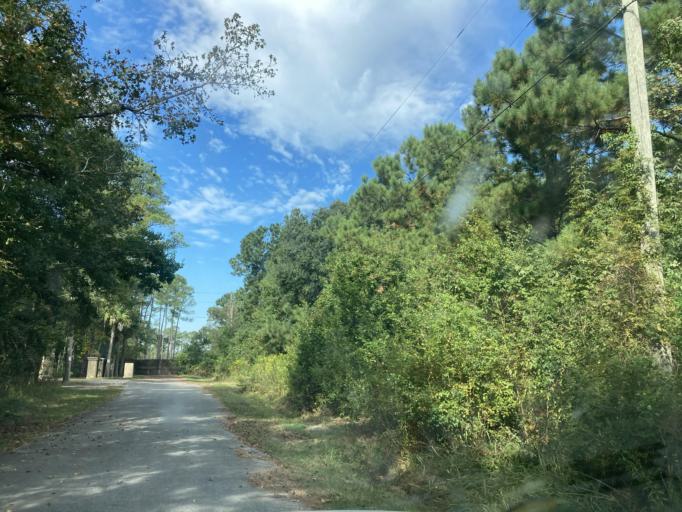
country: US
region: Mississippi
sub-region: Jackson County
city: Saint Martin
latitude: 30.4311
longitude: -88.8615
